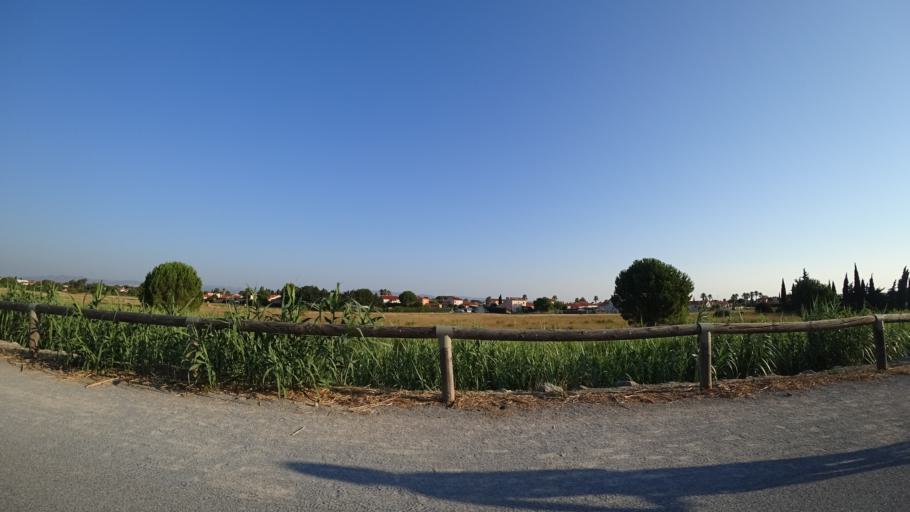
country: FR
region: Languedoc-Roussillon
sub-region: Departement des Pyrenees-Orientales
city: Saint-Laurent-de-la-Salanque
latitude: 42.7662
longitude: 2.9971
